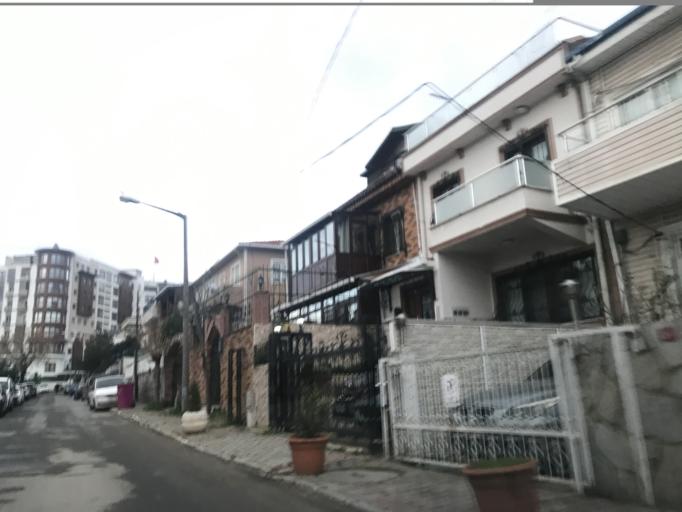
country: TR
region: Istanbul
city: Istanbul
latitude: 41.0406
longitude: 28.9241
